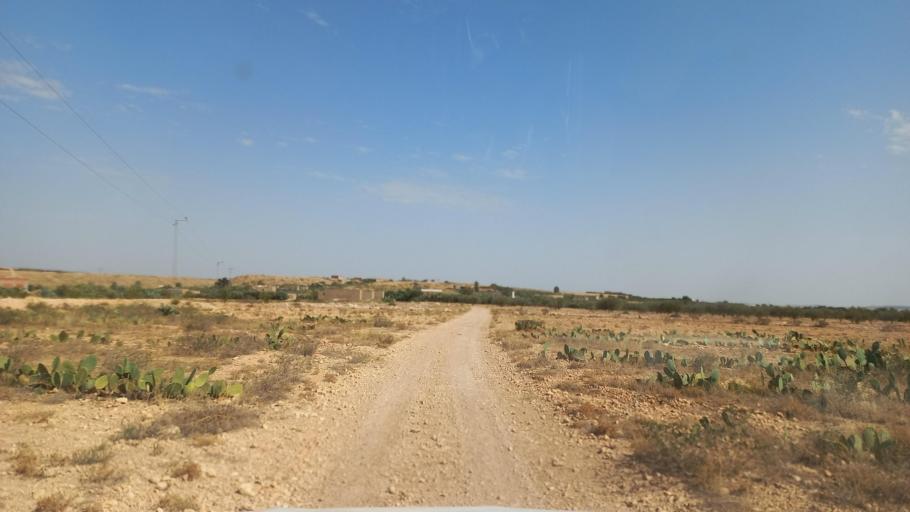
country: TN
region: Al Qasrayn
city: Kasserine
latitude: 35.2789
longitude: 8.9646
